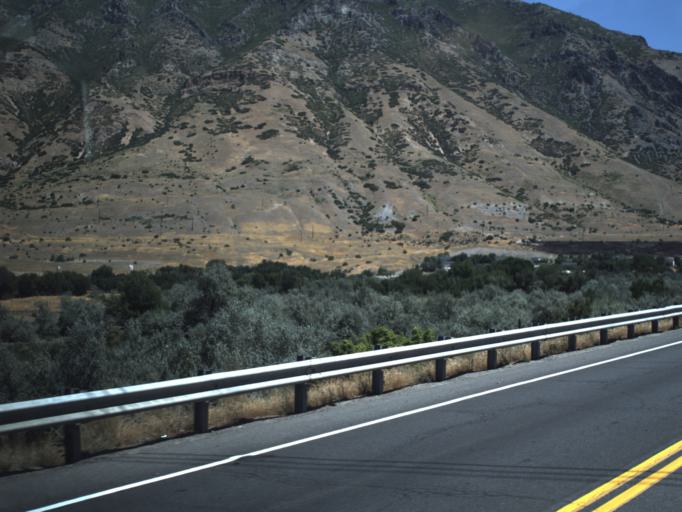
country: US
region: Utah
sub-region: Utah County
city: Springville
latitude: 40.1863
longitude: -111.6216
